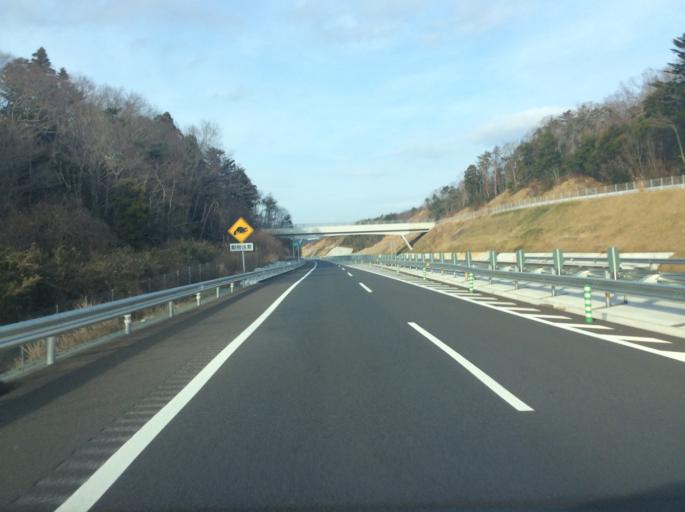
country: JP
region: Fukushima
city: Namie
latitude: 37.4151
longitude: 140.9623
